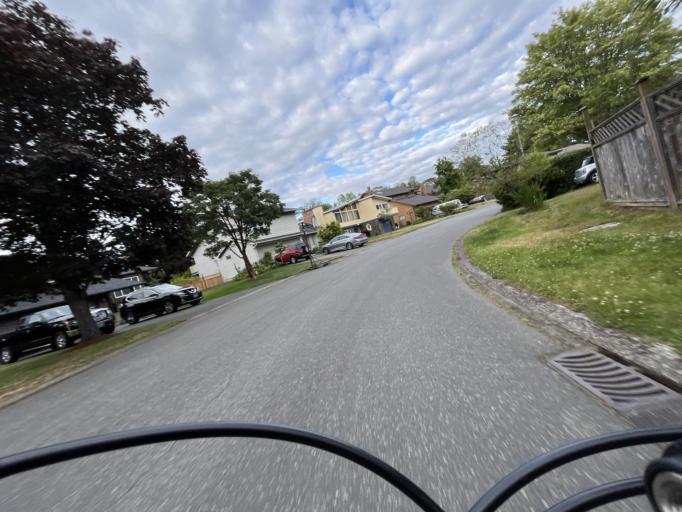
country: CA
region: British Columbia
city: Oak Bay
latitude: 48.4836
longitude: -123.3411
